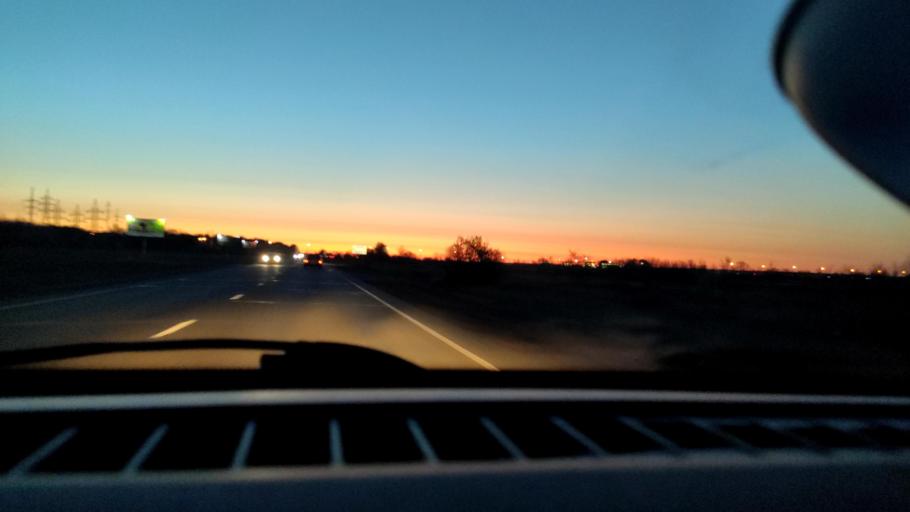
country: RU
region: Samara
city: Samara
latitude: 53.1282
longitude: 50.1613
